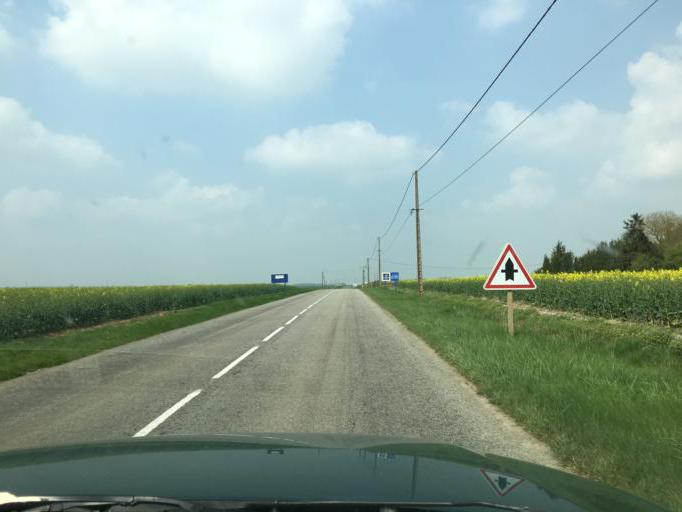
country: FR
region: Centre
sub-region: Departement du Loir-et-Cher
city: Ouzouer-le-Marche
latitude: 47.8414
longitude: 1.5407
